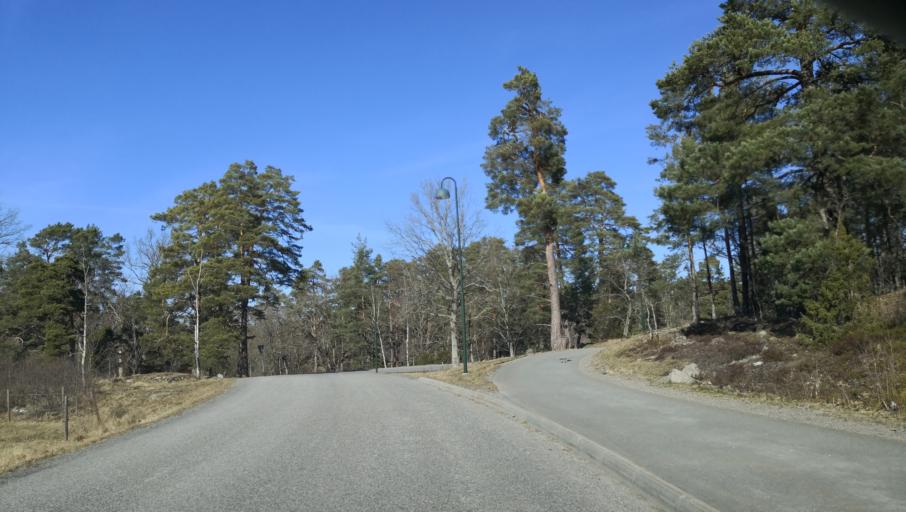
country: SE
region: Stockholm
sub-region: Varmdo Kommun
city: Gustavsberg
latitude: 59.3094
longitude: 18.3551
